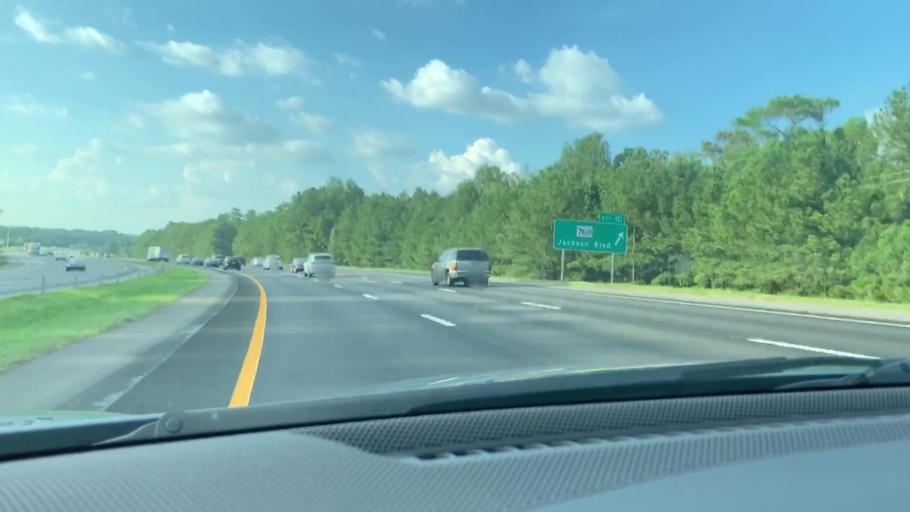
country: US
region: South Carolina
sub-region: Richland County
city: Forest Acres
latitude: 33.9902
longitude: -80.9534
